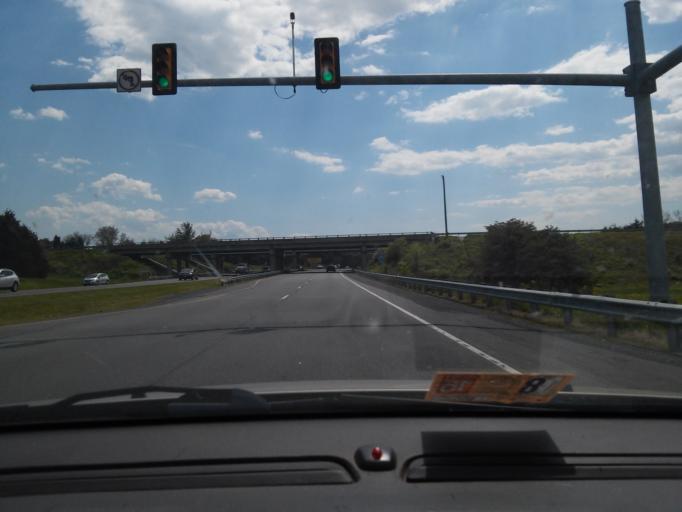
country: US
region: Virginia
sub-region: Warren County
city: Front Royal
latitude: 38.9622
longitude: -78.1922
